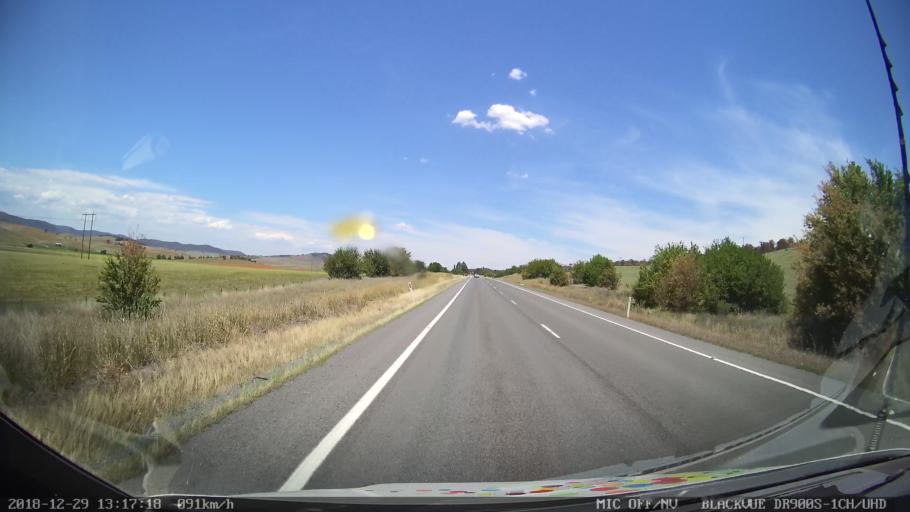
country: AU
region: Australian Capital Territory
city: Macarthur
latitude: -35.7356
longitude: 149.1607
